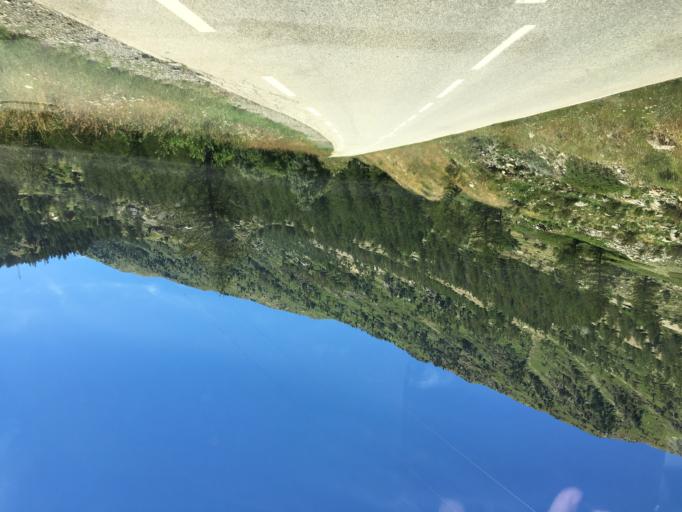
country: IT
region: Piedmont
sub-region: Provincia di Cuneo
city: Vinadio
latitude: 44.2094
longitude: 7.1019
